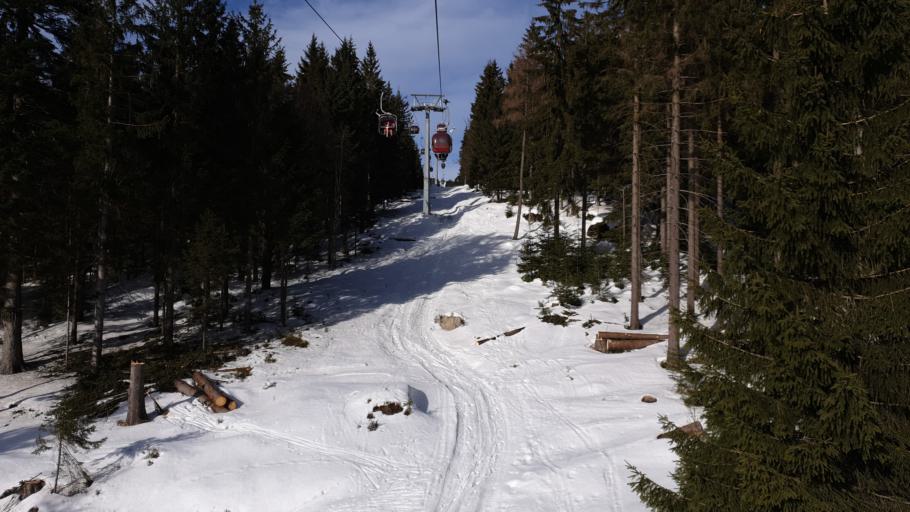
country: DE
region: Bavaria
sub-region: Upper Franconia
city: Bischofsgrun
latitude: 50.0178
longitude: 11.8084
